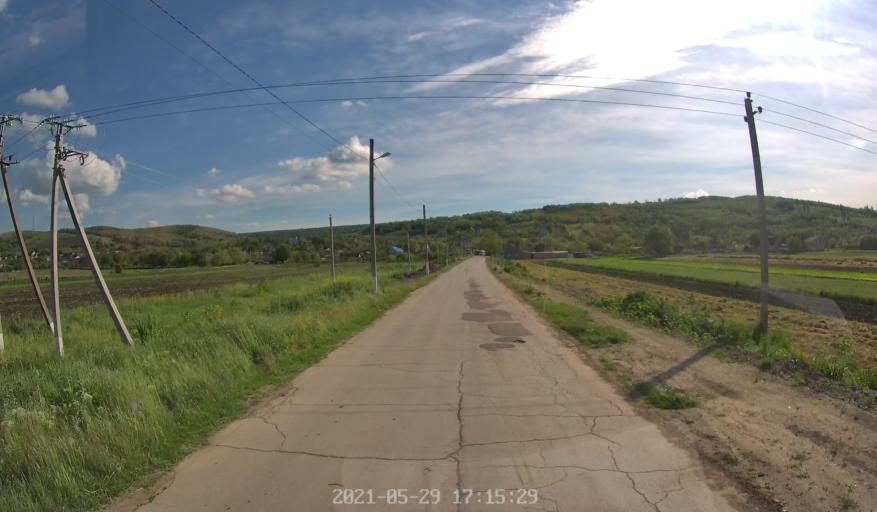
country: MD
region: Laloveni
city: Ialoveni
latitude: 46.8313
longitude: 28.8452
